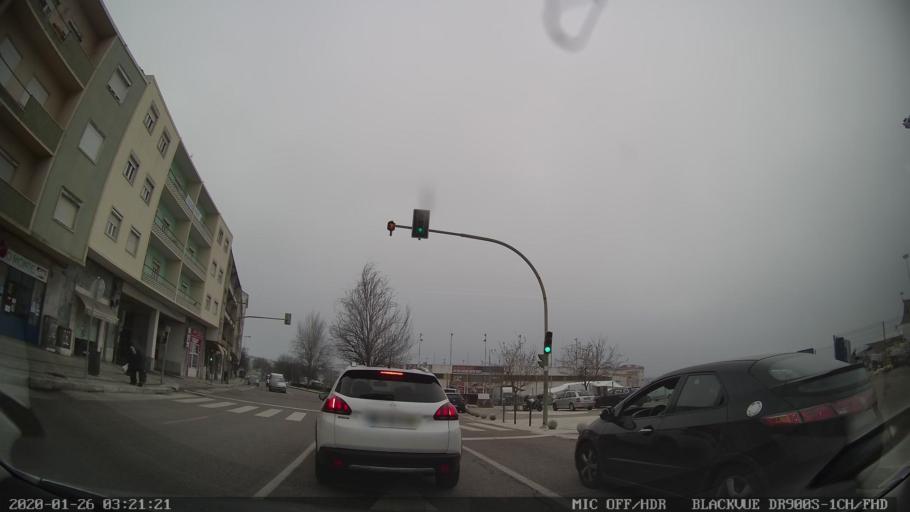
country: PT
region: Santarem
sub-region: Santarem
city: Santarem
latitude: 39.2301
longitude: -8.6877
